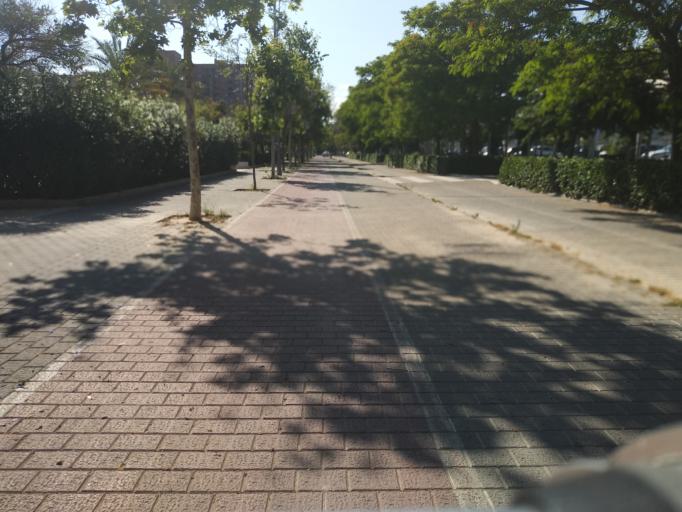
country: ES
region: Valencia
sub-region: Provincia de Valencia
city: Alboraya
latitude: 39.4789
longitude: -0.3488
